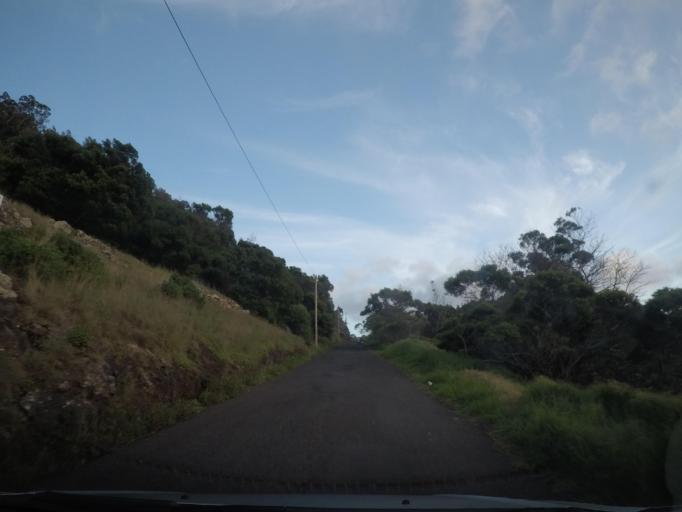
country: PT
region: Madeira
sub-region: Machico
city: Canical
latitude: 32.7263
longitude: -16.7605
